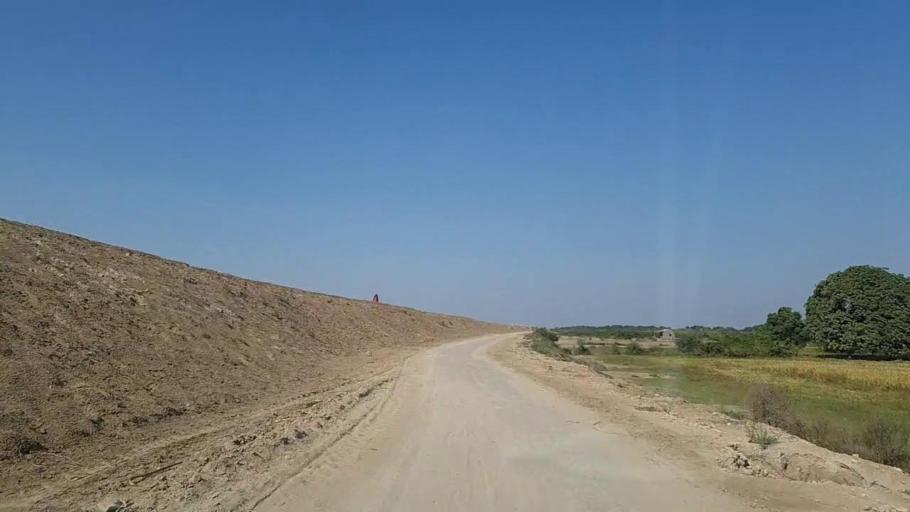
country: PK
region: Sindh
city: Chuhar Jamali
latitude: 24.5600
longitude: 68.0280
